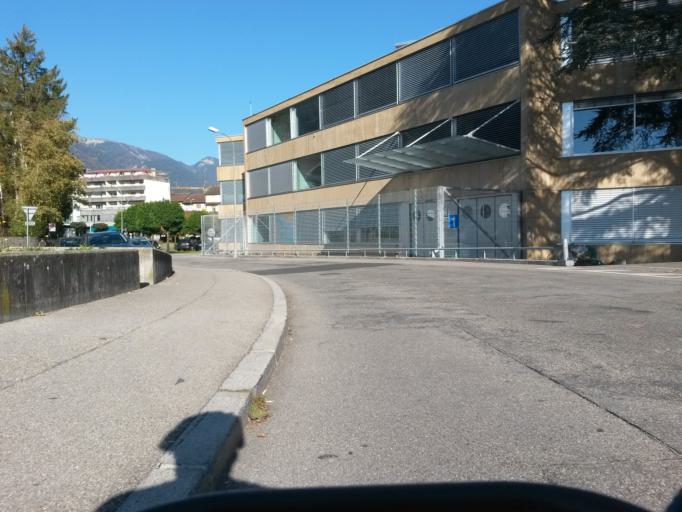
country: CH
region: Solothurn
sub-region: Bezirk Lebern
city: Grenchen
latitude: 47.1885
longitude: 7.3961
